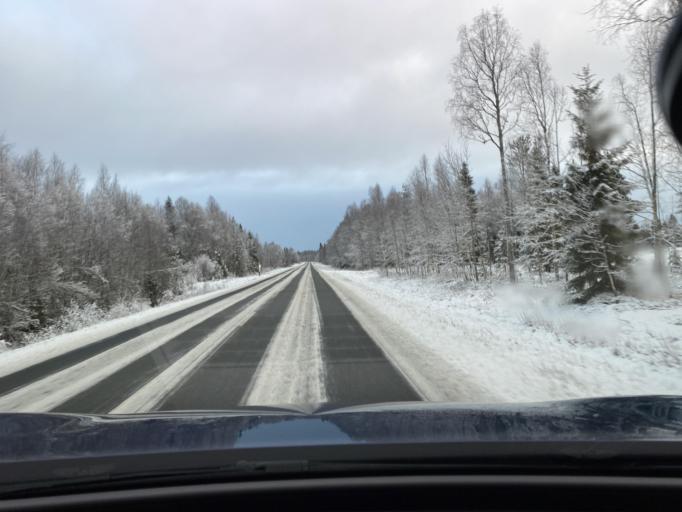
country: FI
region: Lapland
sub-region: Rovaniemi
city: Ranua
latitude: 65.9614
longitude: 26.0475
